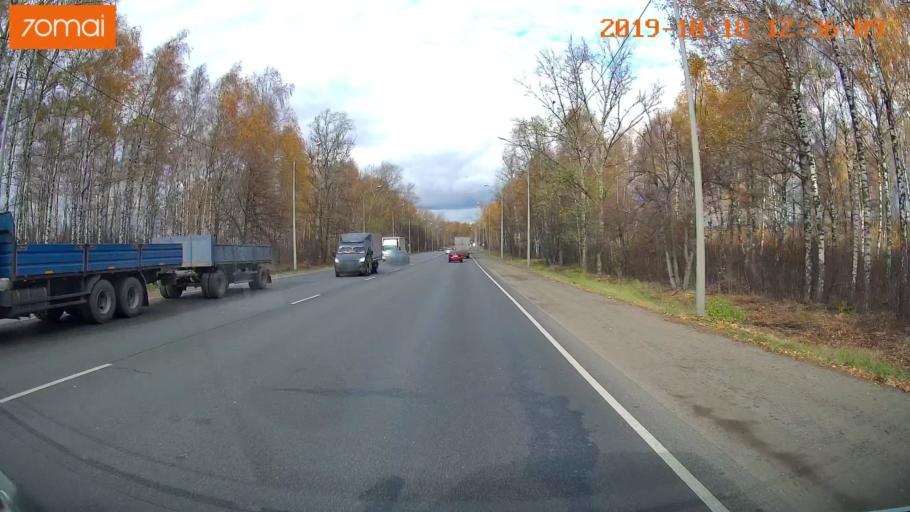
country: RU
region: Rjazan
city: Ryazan'
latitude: 54.6321
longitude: 39.6344
